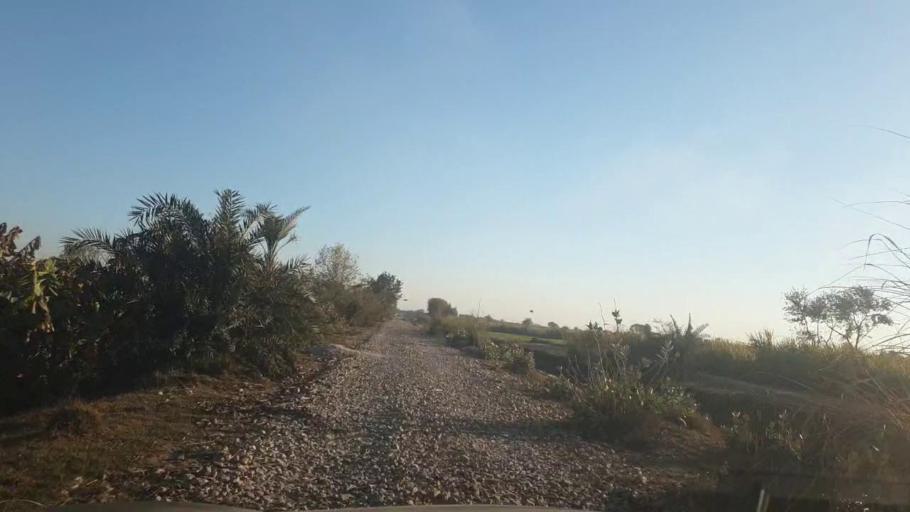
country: PK
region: Sindh
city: Ghotki
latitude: 28.0140
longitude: 69.2682
